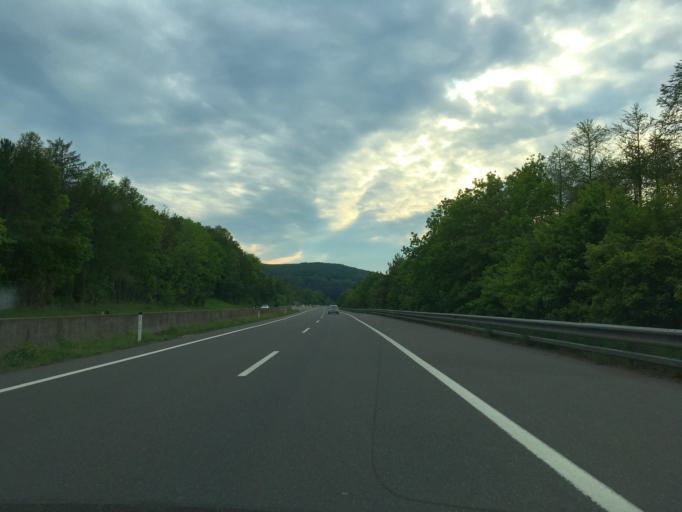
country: AT
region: Lower Austria
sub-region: Politischer Bezirk Wien-Umgebung
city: Wolfsgraben
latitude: 48.1761
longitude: 16.1138
